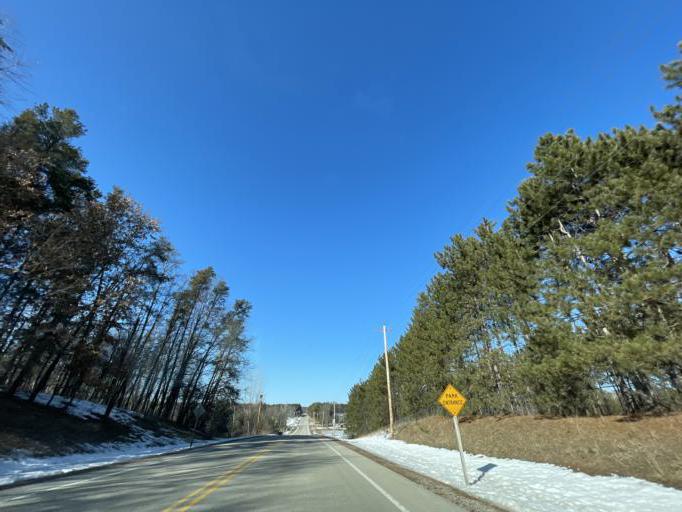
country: US
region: Wisconsin
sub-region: Brown County
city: Suamico
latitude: 44.6572
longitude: -88.0903
